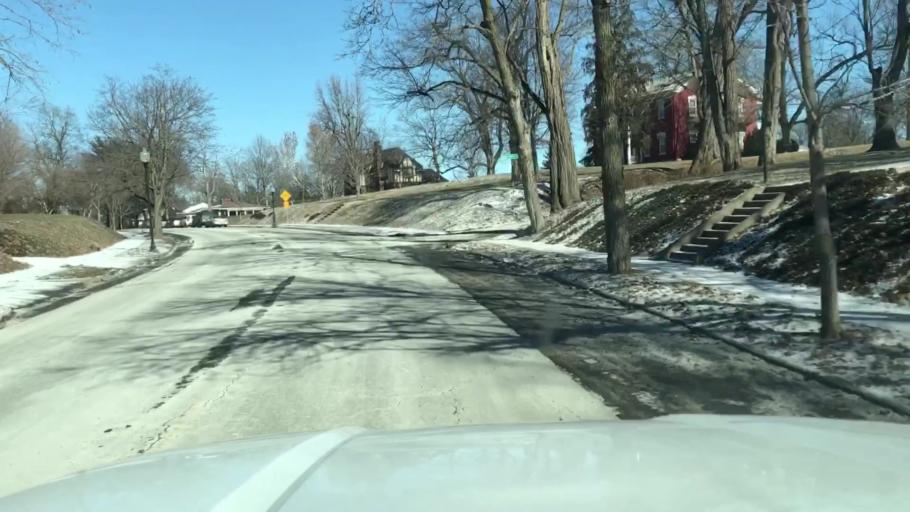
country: US
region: Missouri
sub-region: Andrew County
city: Country Club Village
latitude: 39.7953
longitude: -94.8194
